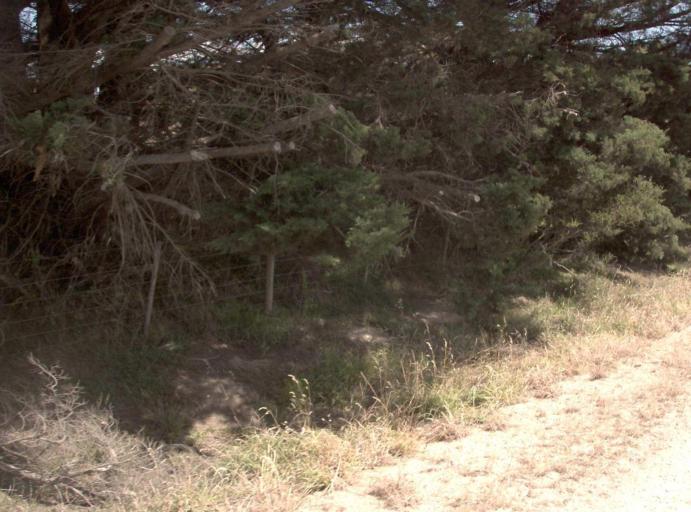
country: AU
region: Victoria
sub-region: Wellington
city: Heyfield
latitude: -38.0292
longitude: 146.8796
